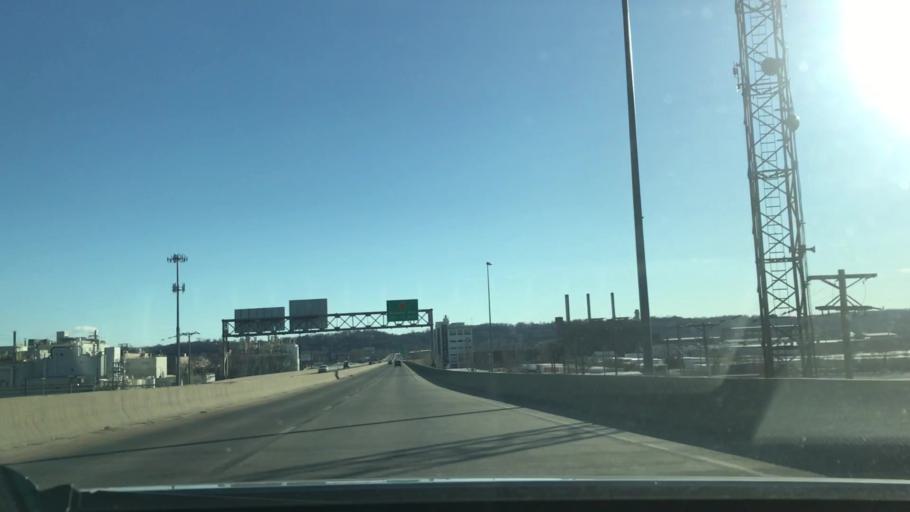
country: US
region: Kansas
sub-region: Wyandotte County
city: Kansas City
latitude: 39.0940
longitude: -94.6494
